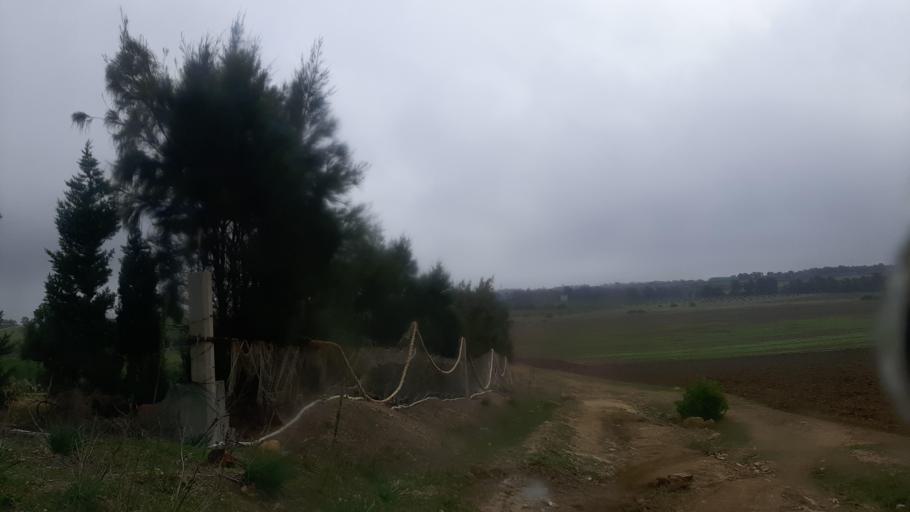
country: TN
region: Nabul
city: Qulaybiyah
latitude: 36.8272
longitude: 11.0357
